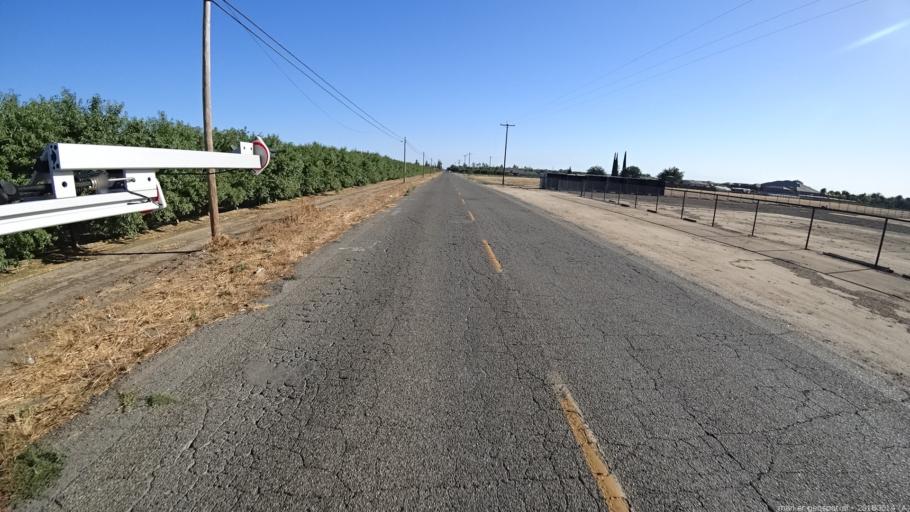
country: US
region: California
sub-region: Madera County
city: Madera
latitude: 36.9422
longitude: -120.1104
